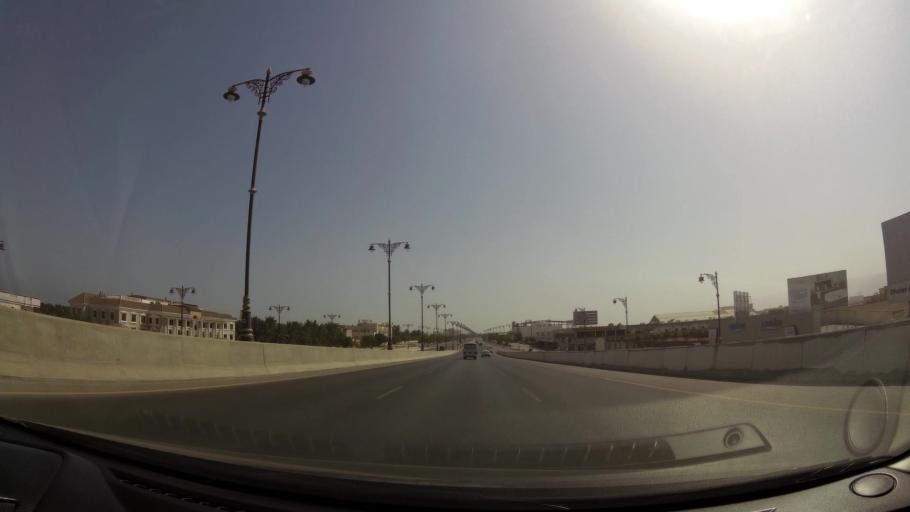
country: OM
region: Zufar
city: Salalah
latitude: 17.0159
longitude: 54.0557
